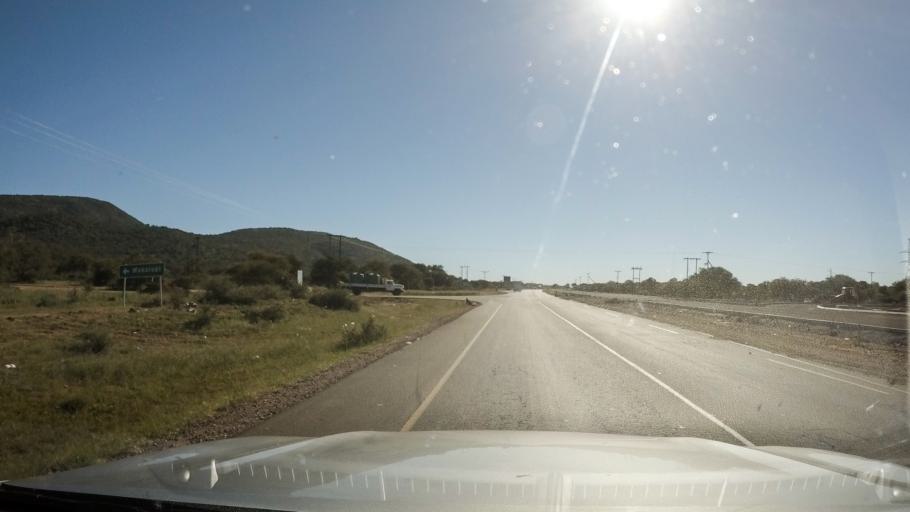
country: BW
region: Kweneng
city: Gabane
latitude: -24.7294
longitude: 25.8493
